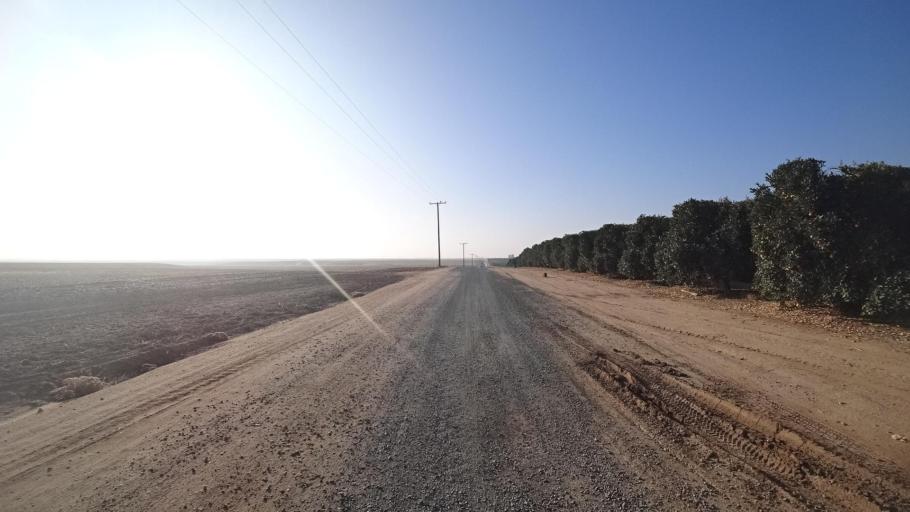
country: US
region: California
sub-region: Tulare County
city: Richgrove
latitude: 35.7760
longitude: -119.0806
